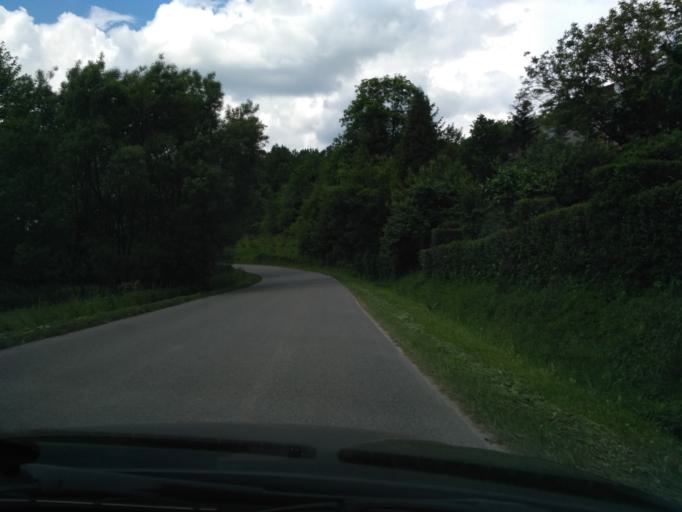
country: PL
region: Subcarpathian Voivodeship
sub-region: Powiat brzozowski
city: Wesola
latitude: 49.8091
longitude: 22.0554
